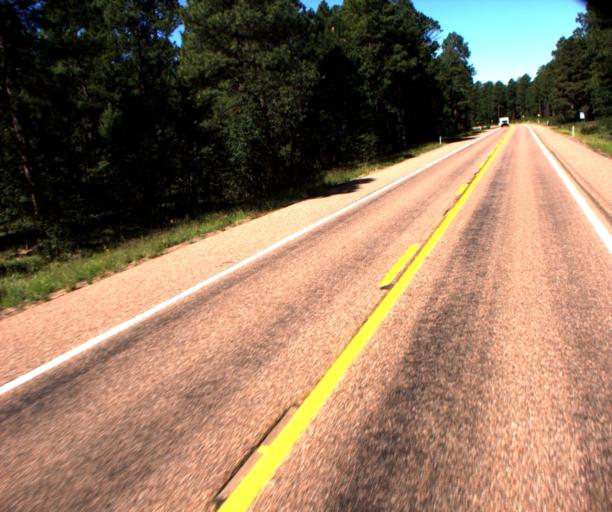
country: US
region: Arizona
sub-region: Navajo County
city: Pinetop-Lakeside
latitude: 34.0796
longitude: -109.8151
